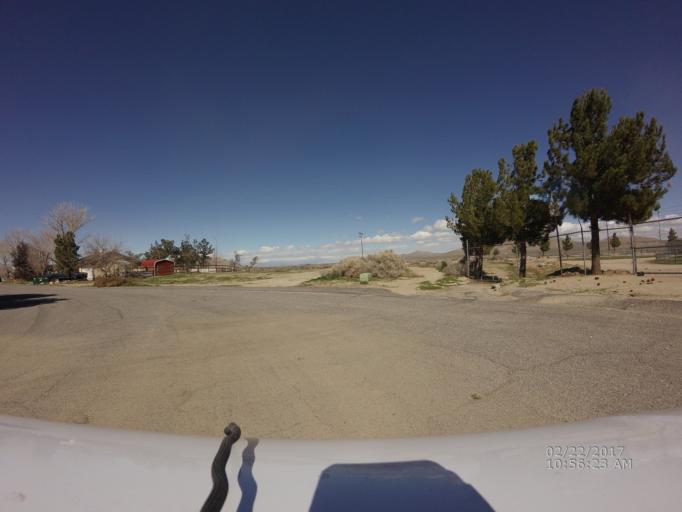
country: US
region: California
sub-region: Los Angeles County
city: Lake Los Angeles
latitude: 34.6303
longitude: -117.8111
